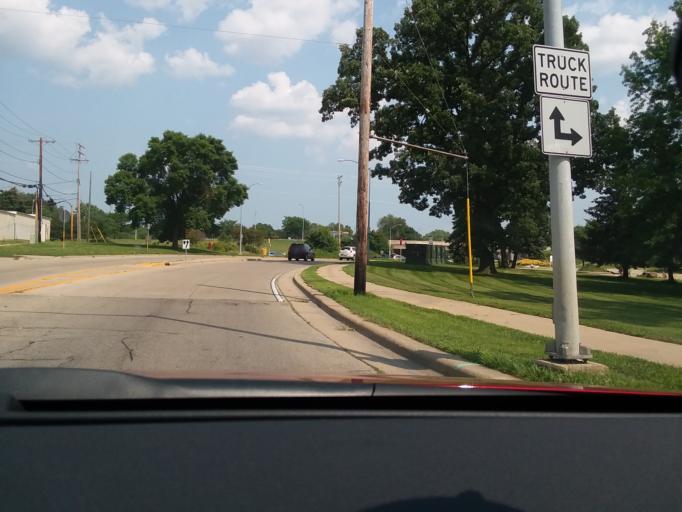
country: US
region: Wisconsin
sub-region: Dane County
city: Maple Bluff
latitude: 43.1142
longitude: -89.3565
